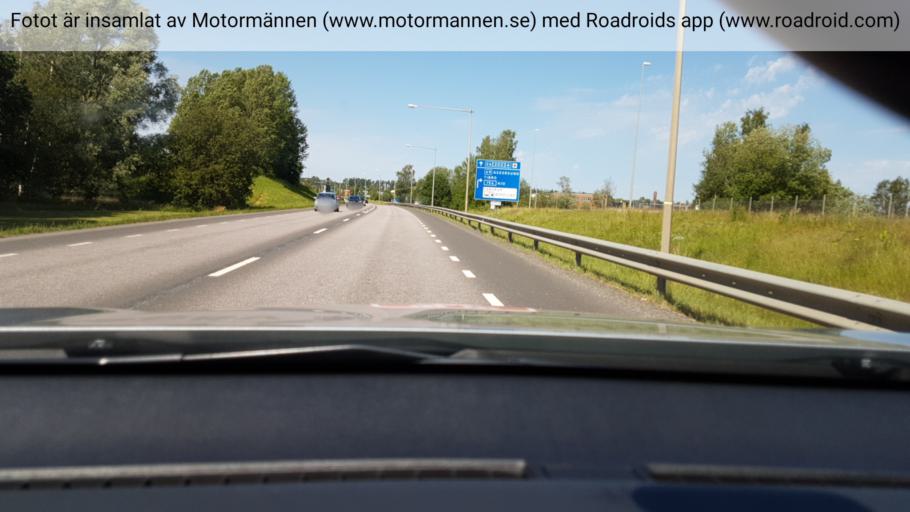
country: SE
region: Vaestra Goetaland
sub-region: Skovde Kommun
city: Skoevde
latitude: 58.3901
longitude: 13.8749
